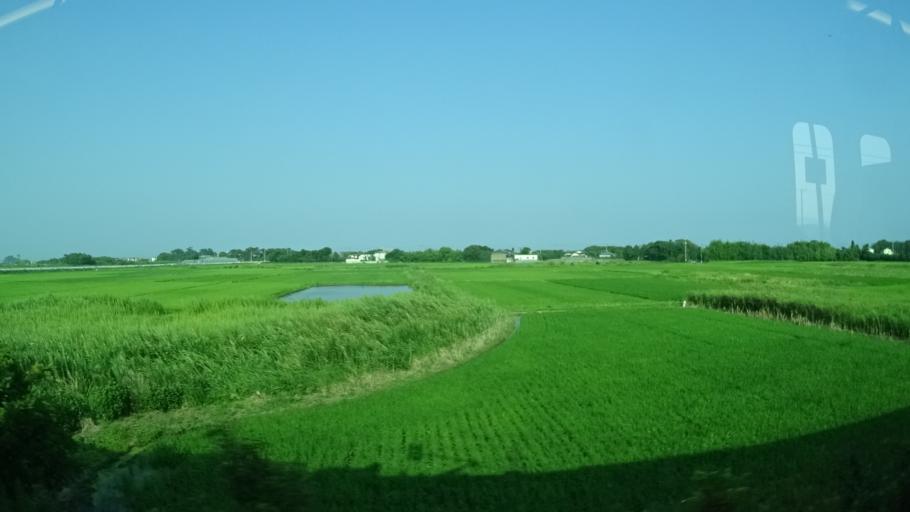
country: JP
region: Ibaraki
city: Kitaibaraki
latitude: 36.7828
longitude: 140.7401
